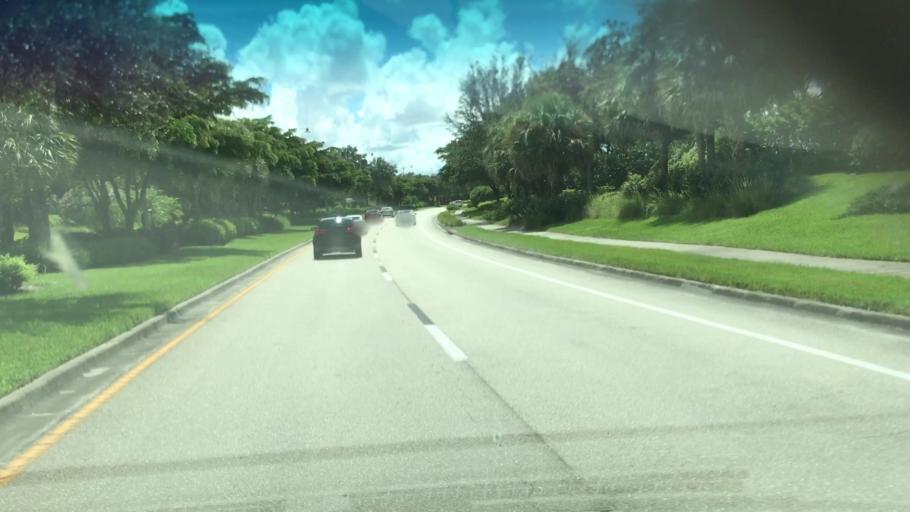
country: US
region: Florida
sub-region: Lee County
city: Estero
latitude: 26.4116
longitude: -81.7841
